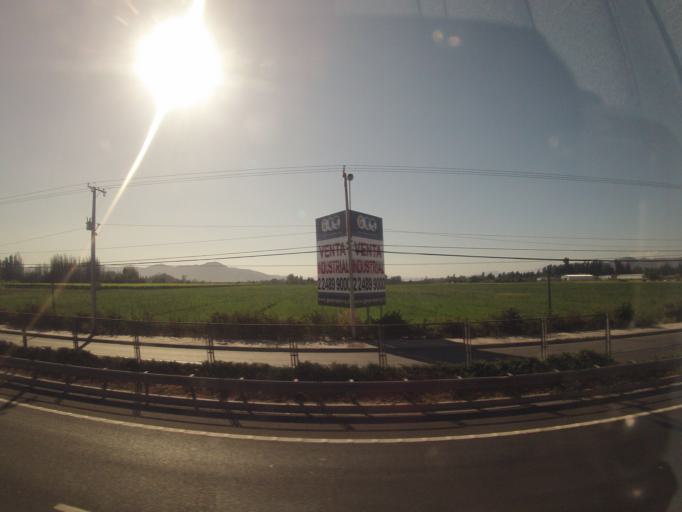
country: CL
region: Santiago Metropolitan
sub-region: Provincia de Maipo
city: San Bernardo
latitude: -33.6618
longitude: -70.7180
